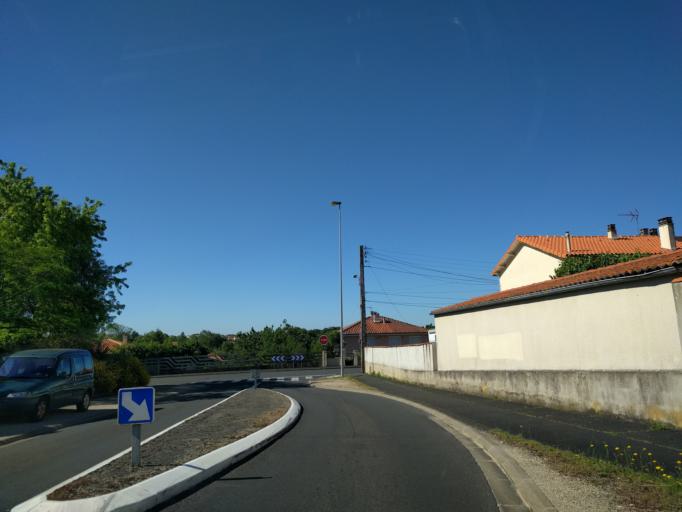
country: FR
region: Poitou-Charentes
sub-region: Departement des Deux-Sevres
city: Niort
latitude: 46.3379
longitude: -0.4401
